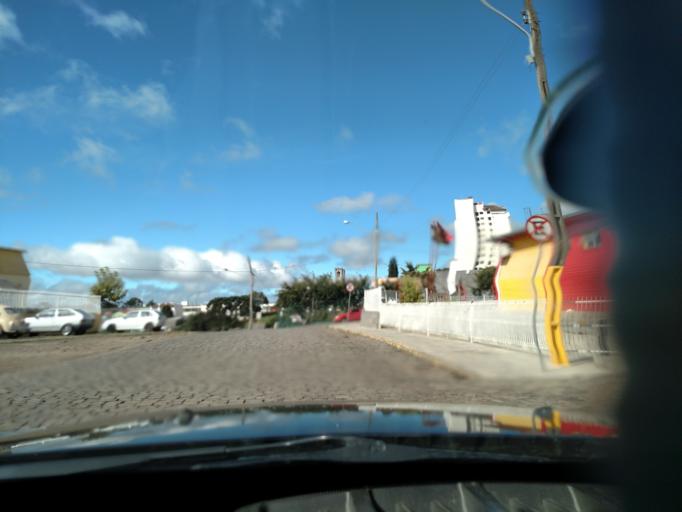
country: BR
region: Santa Catarina
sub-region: Sao Joaquim
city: Sao Joaquim
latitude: -28.2917
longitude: -49.9305
